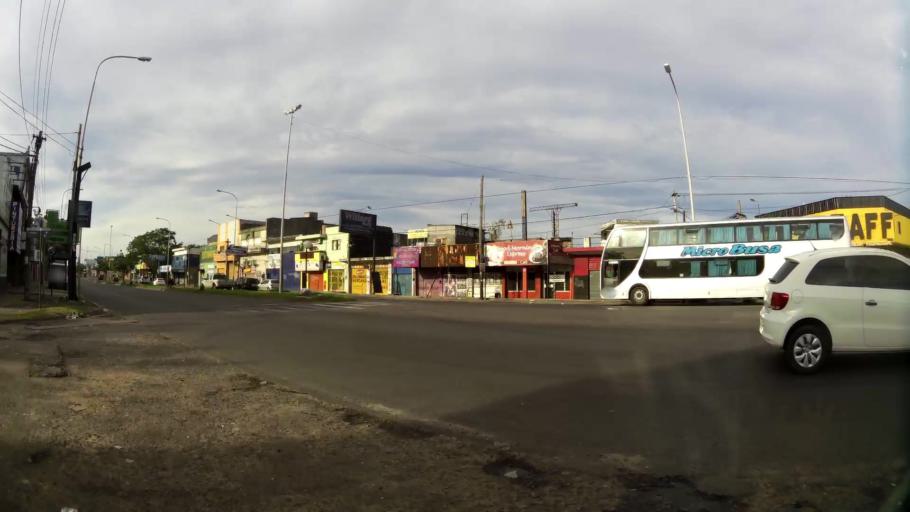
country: AR
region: Buenos Aires
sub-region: Partido de Moron
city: Moron
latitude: -34.6397
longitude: -58.6258
